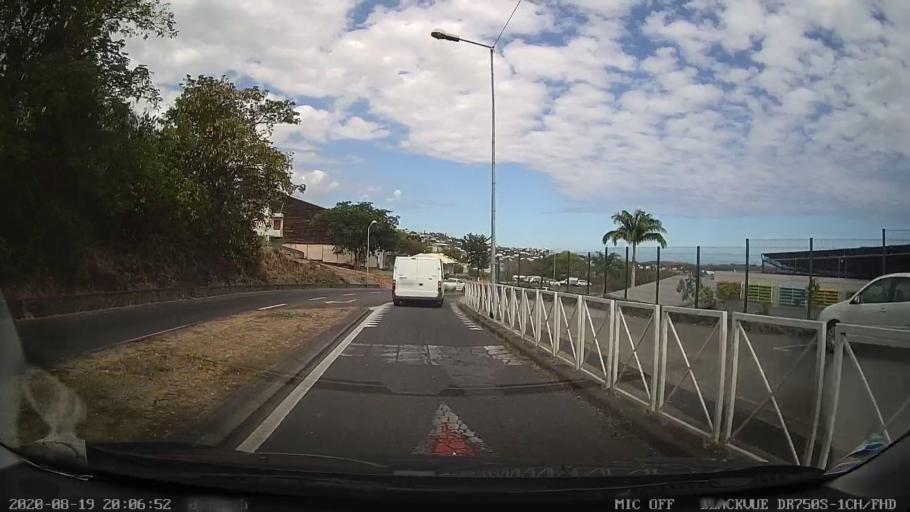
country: RE
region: Reunion
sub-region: Reunion
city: La Possession
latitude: -20.9577
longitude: 55.3344
